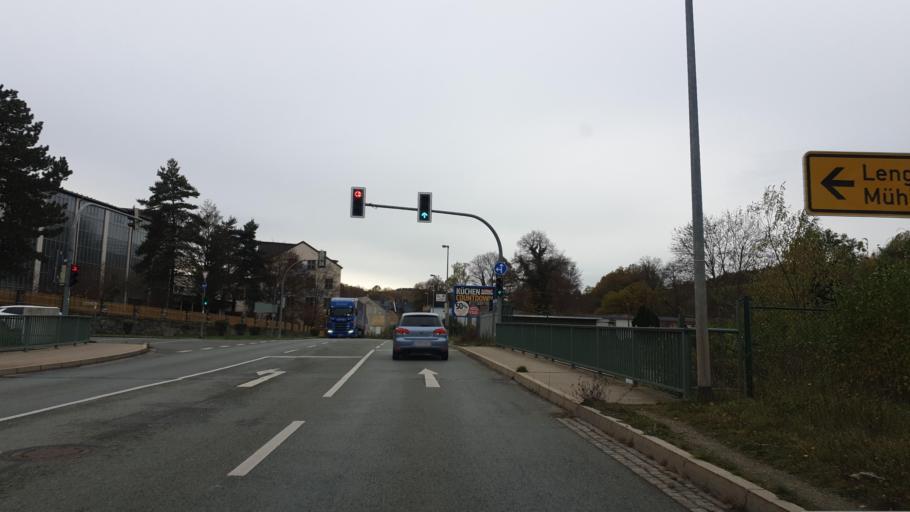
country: DE
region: Saxony
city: Mylau
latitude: 50.6223
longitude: 12.2611
